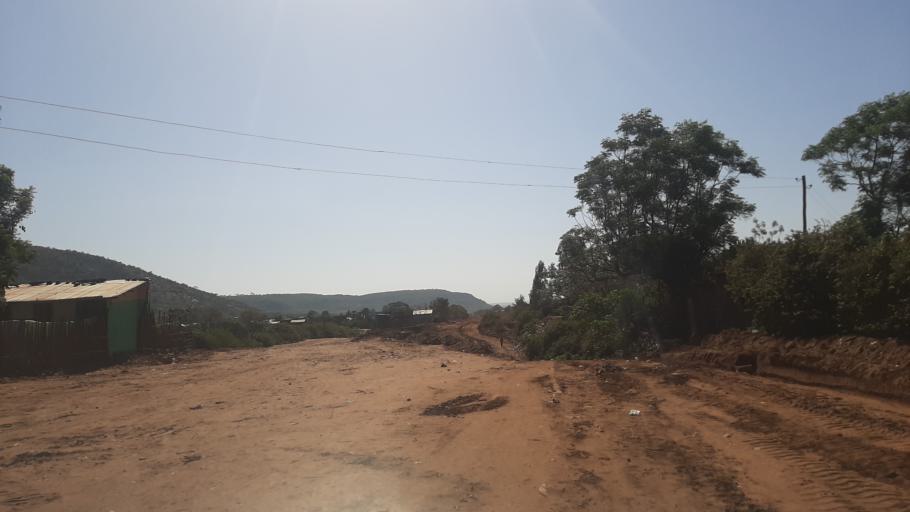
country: ET
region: Oromiya
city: Yabelo
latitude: 4.8942
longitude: 38.0997
